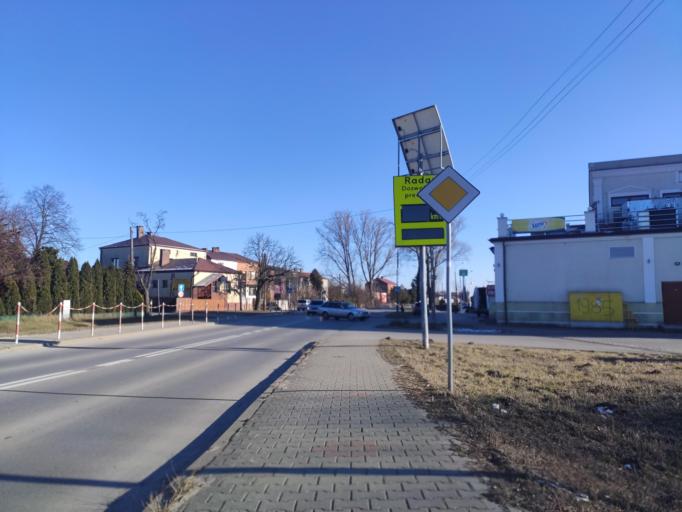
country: PL
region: Lublin Voivodeship
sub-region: Powiat lubartowski
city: Kock
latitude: 51.6430
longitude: 22.4469
